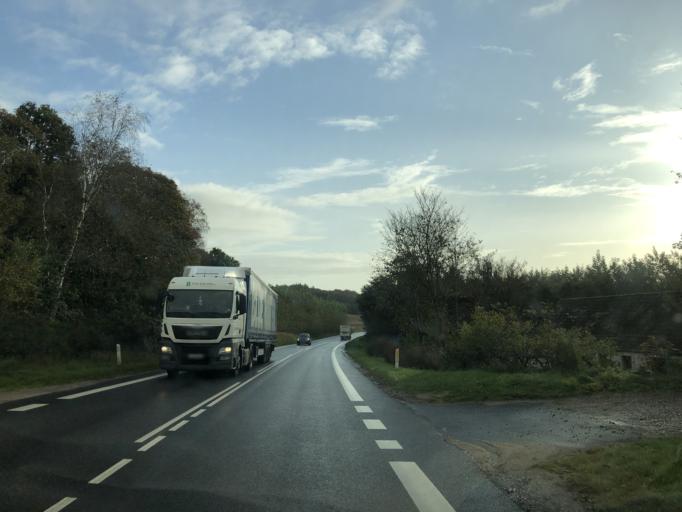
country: DK
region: North Denmark
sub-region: Mariagerfjord Kommune
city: Hobro
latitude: 56.6155
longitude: 9.6671
